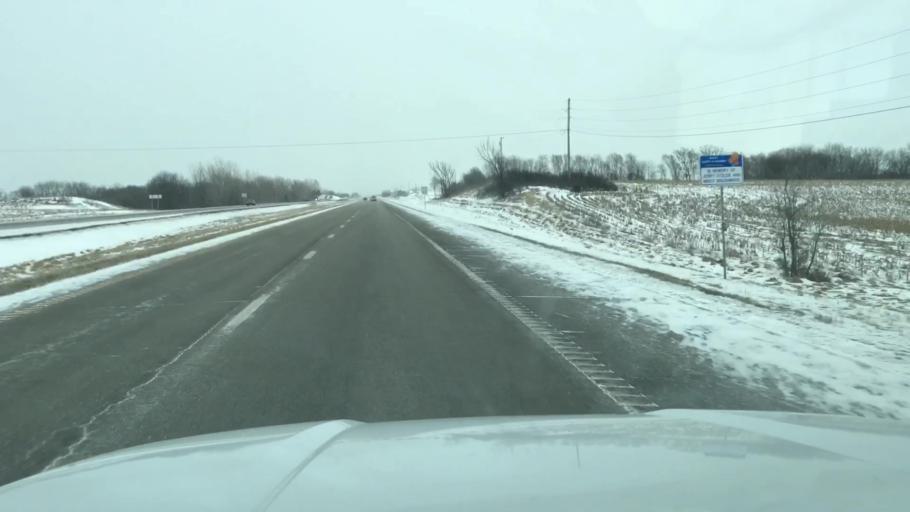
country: US
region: Missouri
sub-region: Clinton County
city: Gower
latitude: 39.7472
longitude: -94.6425
